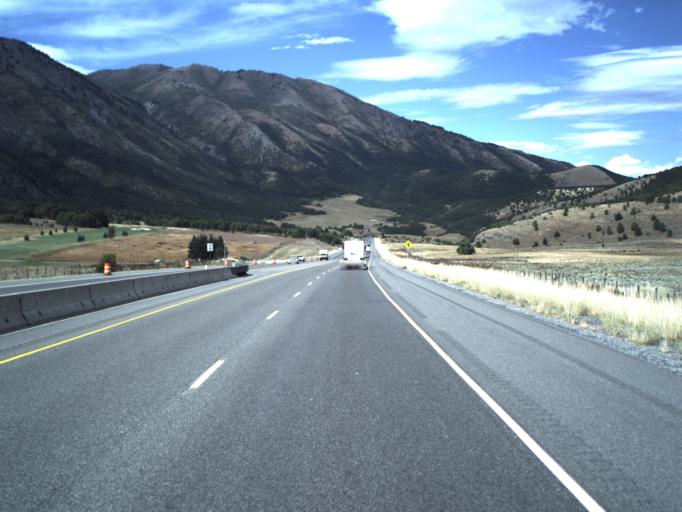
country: US
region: Utah
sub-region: Cache County
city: Wellsville
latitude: 41.5808
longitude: -111.9740
